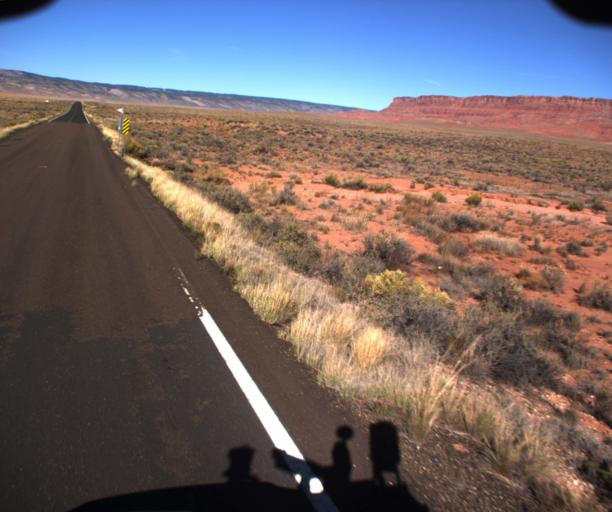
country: US
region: Arizona
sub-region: Coconino County
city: Page
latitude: 36.7039
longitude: -111.9425
